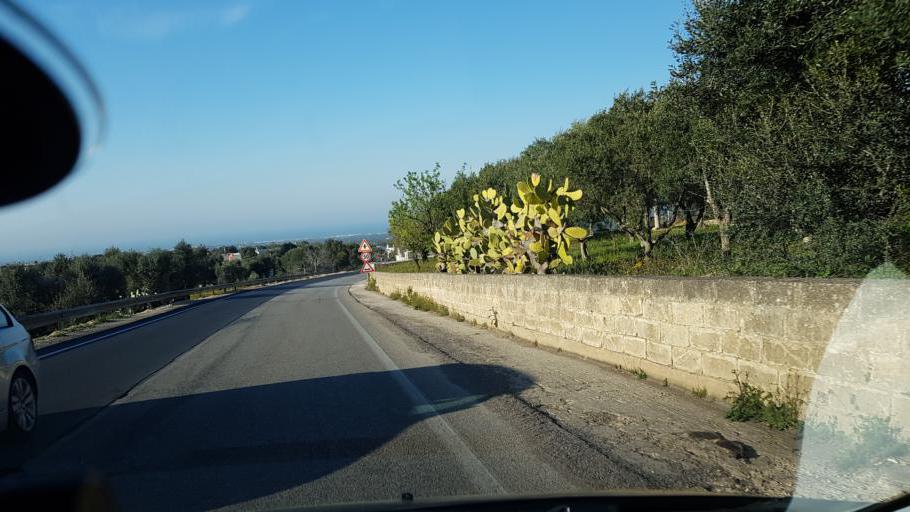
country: IT
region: Apulia
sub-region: Provincia di Brindisi
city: Ostuni
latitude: 40.7306
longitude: 17.5901
